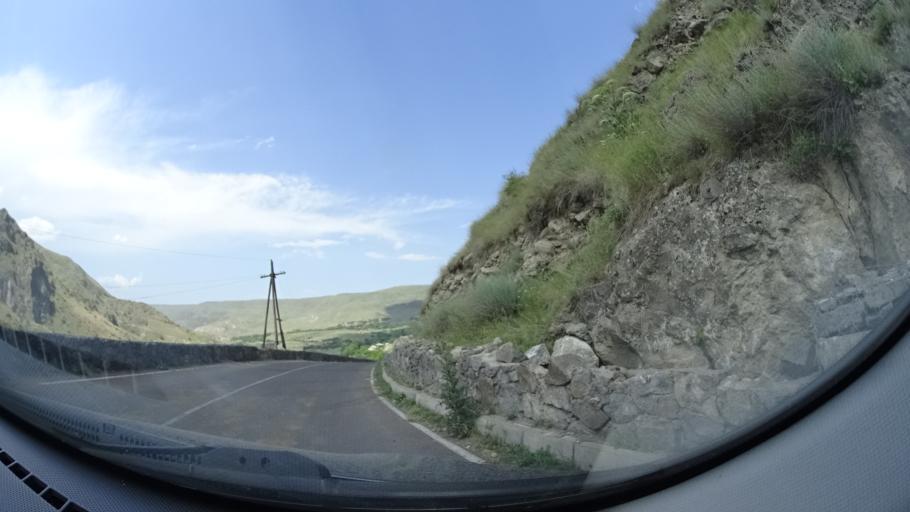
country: GE
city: Akhalk'alak'i
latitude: 41.3963
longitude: 43.3217
